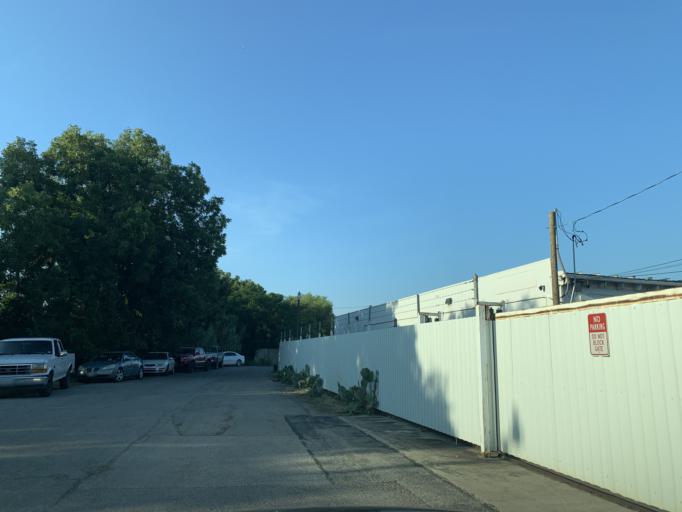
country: US
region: Texas
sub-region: Tarrant County
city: Fort Worth
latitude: 32.7586
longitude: -97.3492
